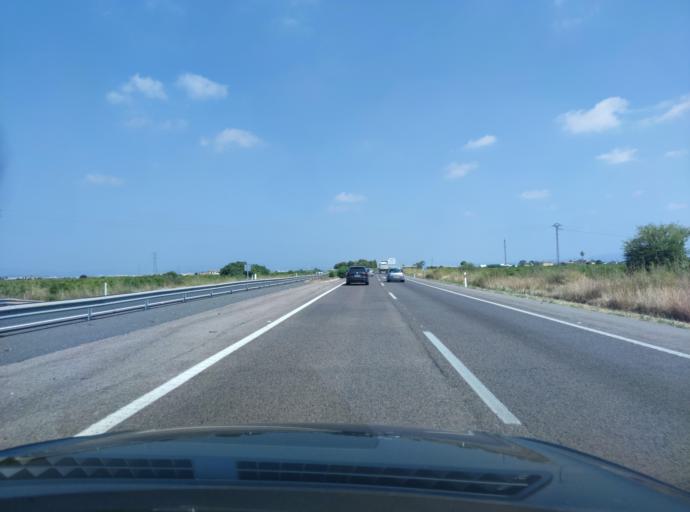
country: ES
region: Valencia
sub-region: Provincia de Castello
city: Alquerias del Nino Perdido
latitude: 39.8902
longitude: -0.1282
